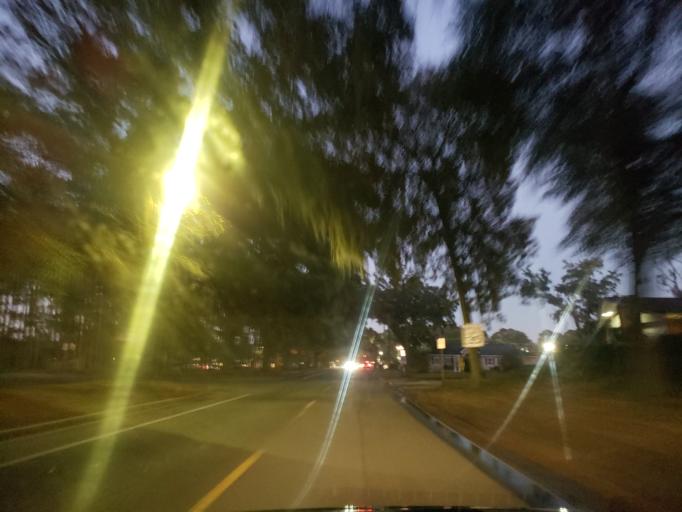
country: US
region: Georgia
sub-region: Chatham County
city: Thunderbolt
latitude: 32.0438
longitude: -81.0774
